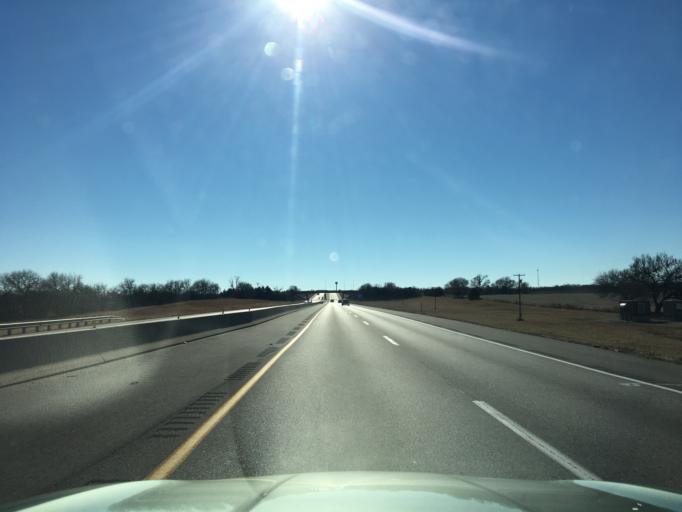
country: US
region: Kansas
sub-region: Sumner County
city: Belle Plaine
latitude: 37.3820
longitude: -97.3242
